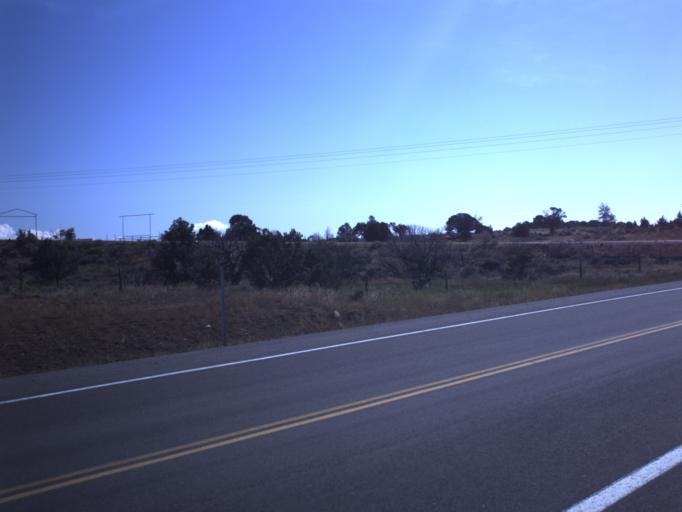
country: US
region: Utah
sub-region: Duchesne County
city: Duchesne
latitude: 40.3584
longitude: -110.3891
